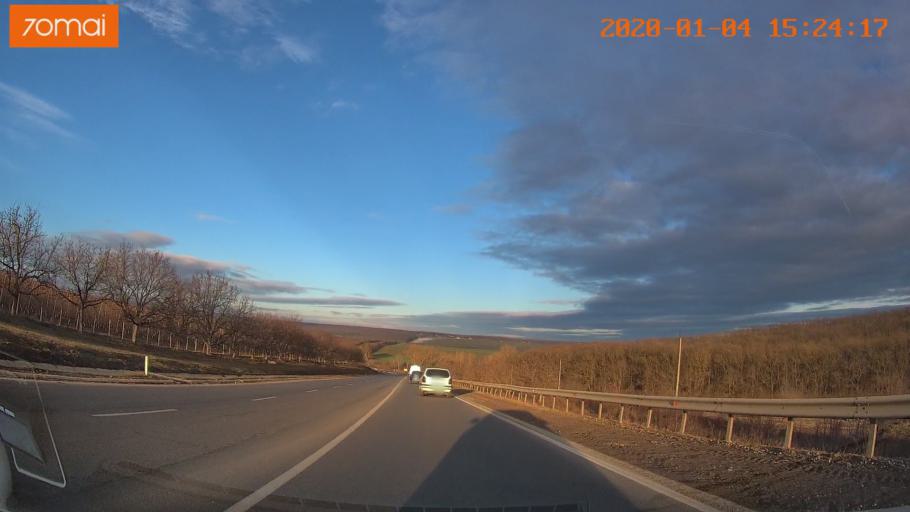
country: MD
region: Orhei
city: Orhei
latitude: 47.2751
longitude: 28.7952
